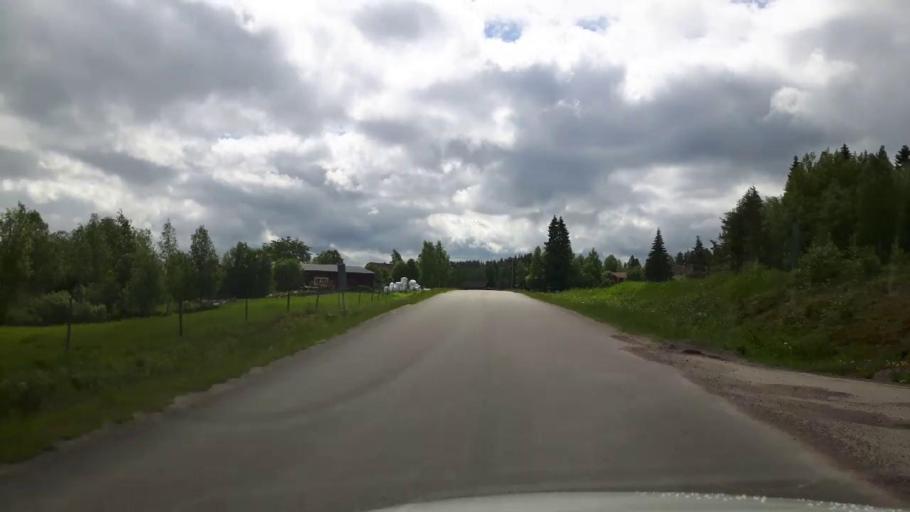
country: SE
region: Gaevleborg
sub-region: Ovanakers Kommun
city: Edsbyn
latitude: 61.3505
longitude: 15.9183
